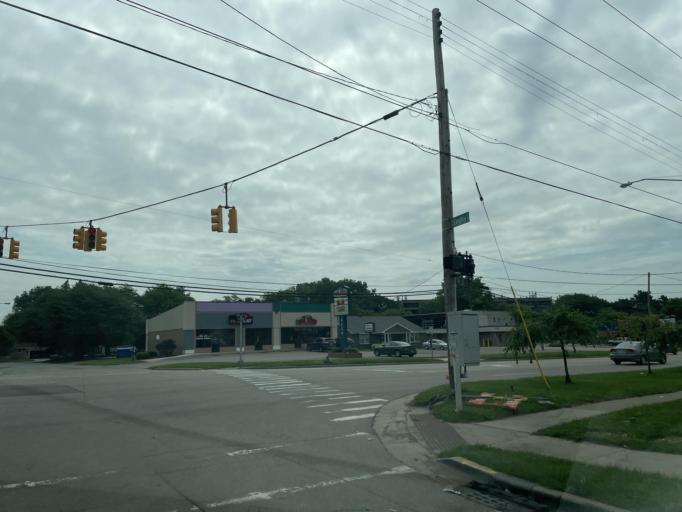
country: US
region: Michigan
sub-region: Kent County
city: Kentwood
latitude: 42.8866
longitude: -85.6264
